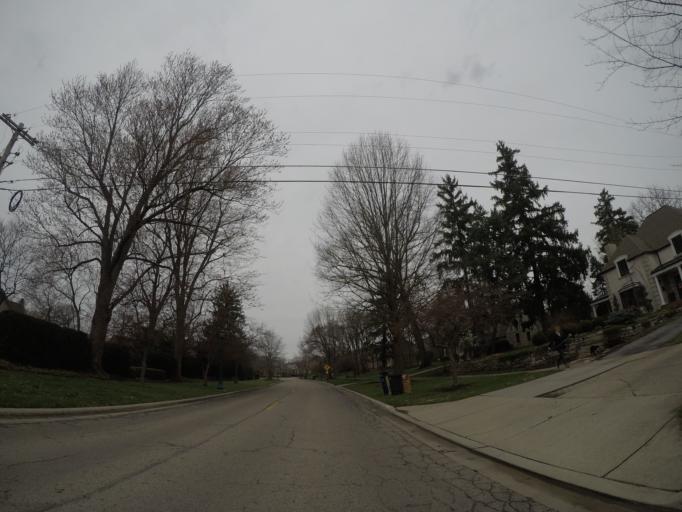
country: US
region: Ohio
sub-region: Franklin County
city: Upper Arlington
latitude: 40.0044
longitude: -83.0681
